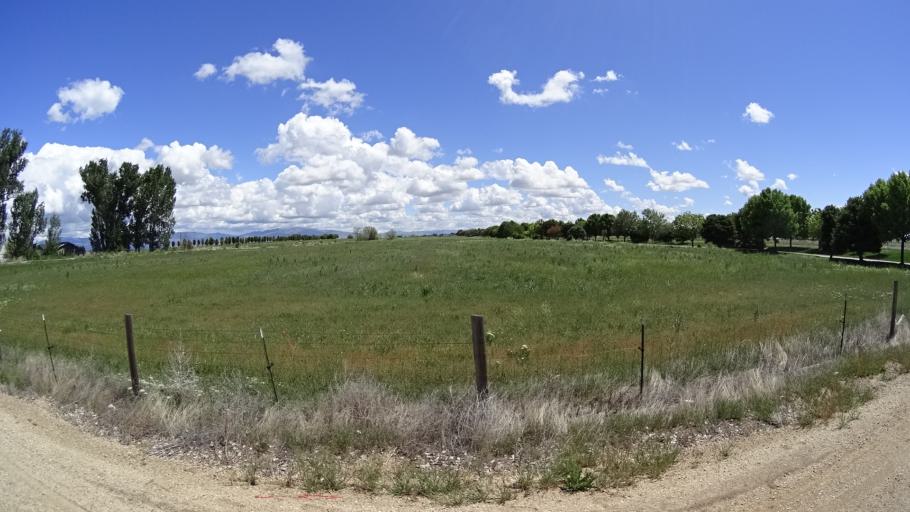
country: US
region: Idaho
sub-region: Ada County
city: Kuna
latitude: 43.5395
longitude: -116.3543
